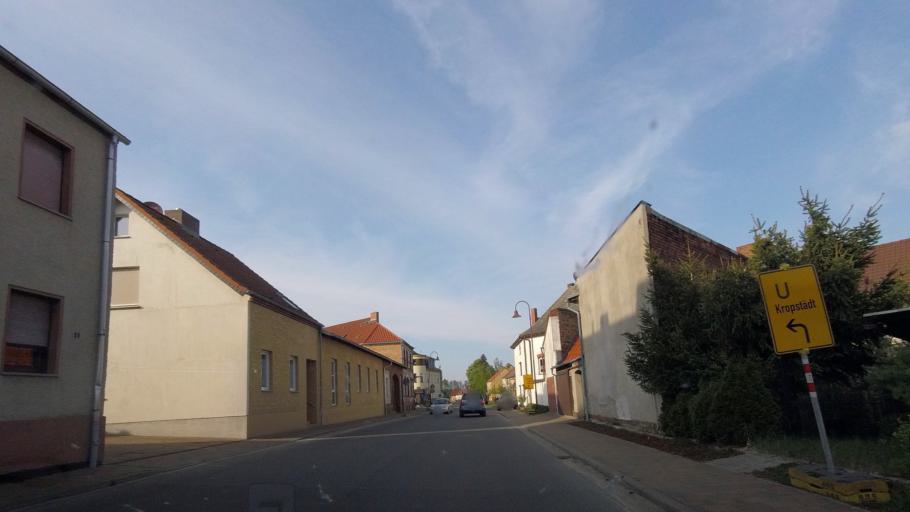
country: DE
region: Saxony-Anhalt
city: Zahna
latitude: 51.9169
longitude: 12.7844
